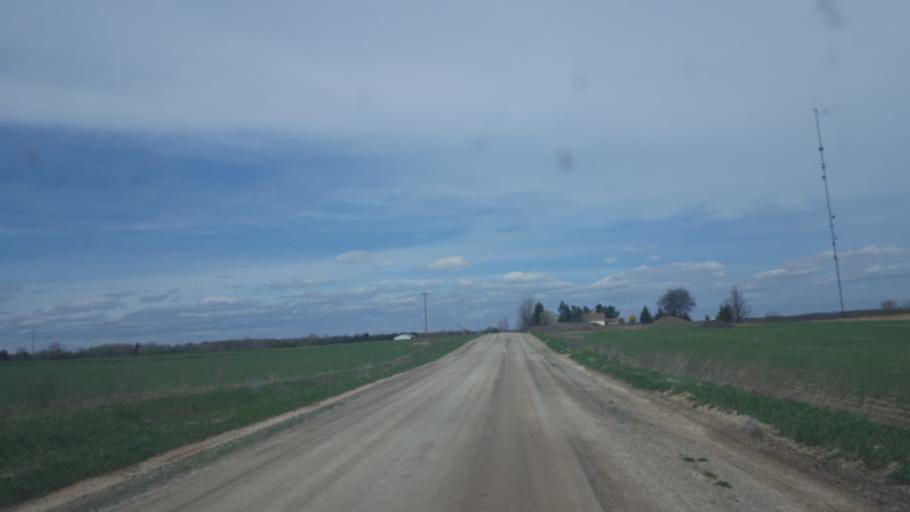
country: US
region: Michigan
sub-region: Isabella County
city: Lake Isabella
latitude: 43.6178
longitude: -84.8880
